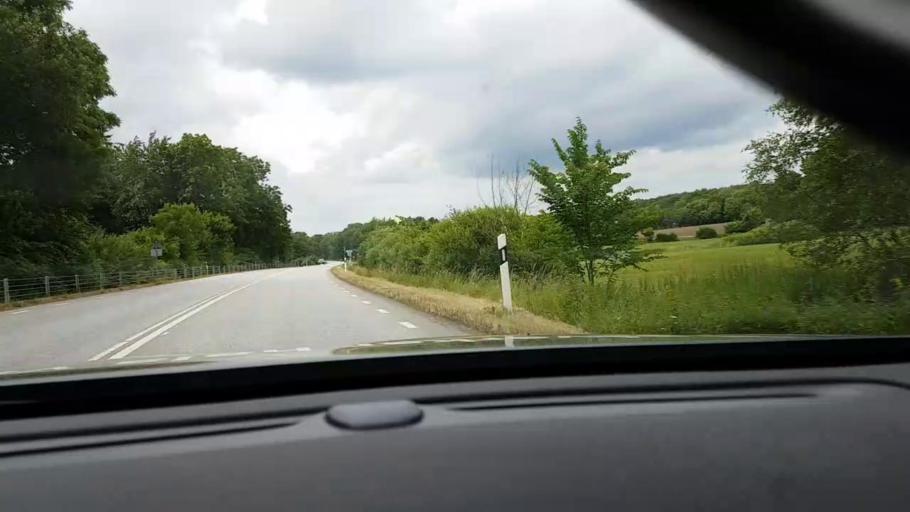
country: SE
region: Skane
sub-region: Horby Kommun
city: Hoerby
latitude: 55.8758
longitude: 13.6320
